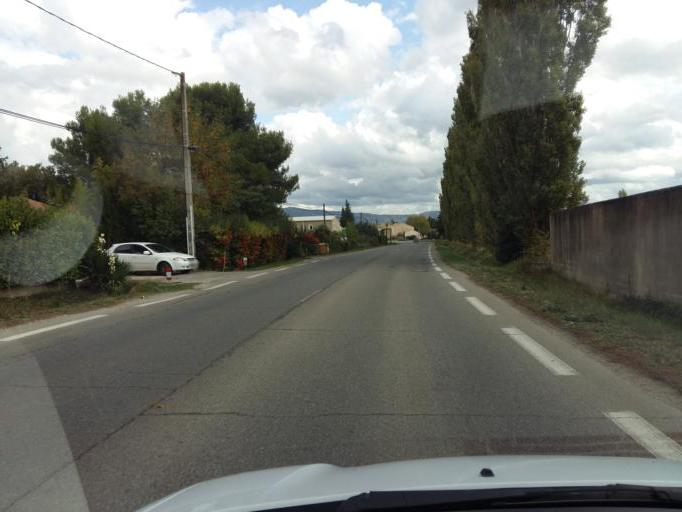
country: FR
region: Provence-Alpes-Cote d'Azur
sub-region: Departement du Vaucluse
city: L'Isle-sur-la-Sorgue
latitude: 43.9126
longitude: 5.0380
